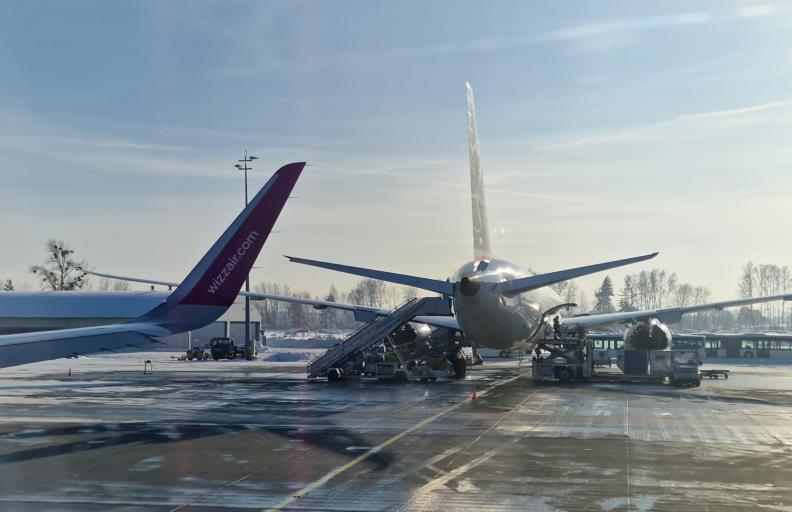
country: PL
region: Silesian Voivodeship
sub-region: Powiat tarnogorski
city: Ozarowice
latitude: 50.4714
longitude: 19.0740
